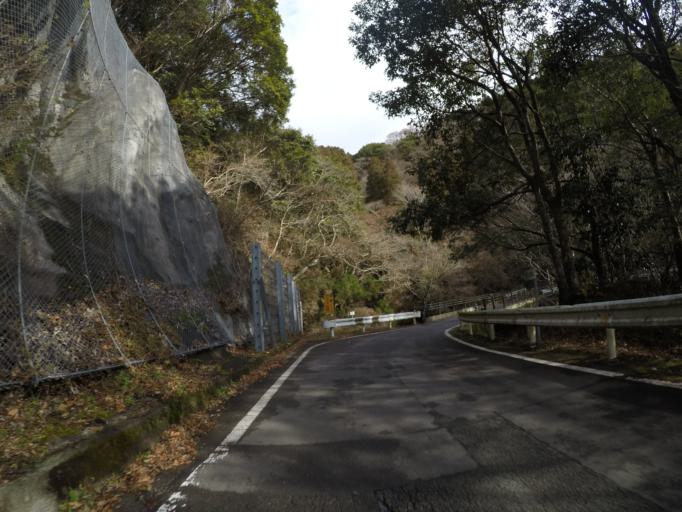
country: JP
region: Shizuoka
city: Heda
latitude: 34.8465
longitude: 138.8533
